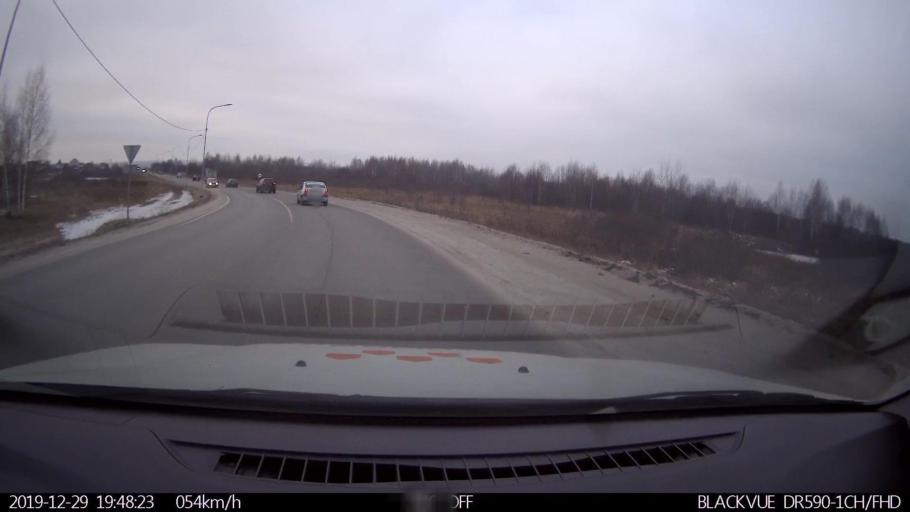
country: RU
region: Nizjnij Novgorod
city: Neklyudovo
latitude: 56.3844
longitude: 44.0096
